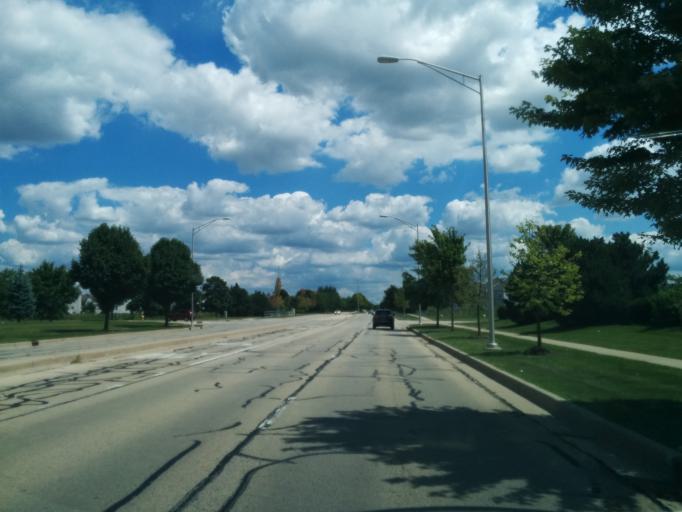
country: US
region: Illinois
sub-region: Will County
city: Romeoville
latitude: 41.6819
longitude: -88.1474
